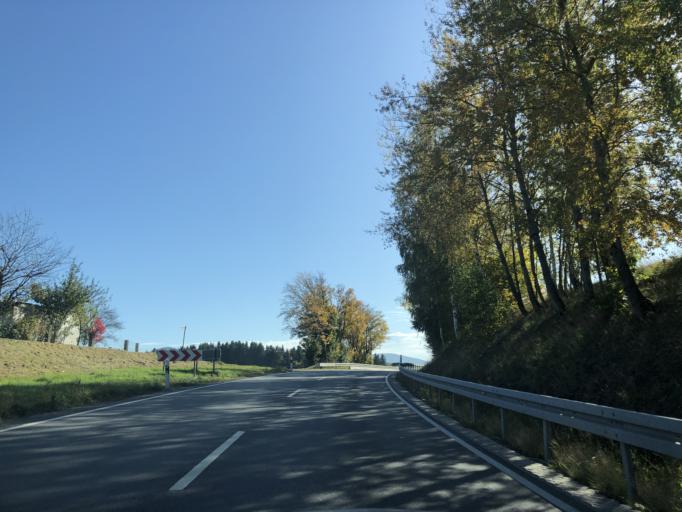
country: DE
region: Bavaria
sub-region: Lower Bavaria
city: Ruhmannsfelden
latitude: 48.9971
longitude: 12.9812
